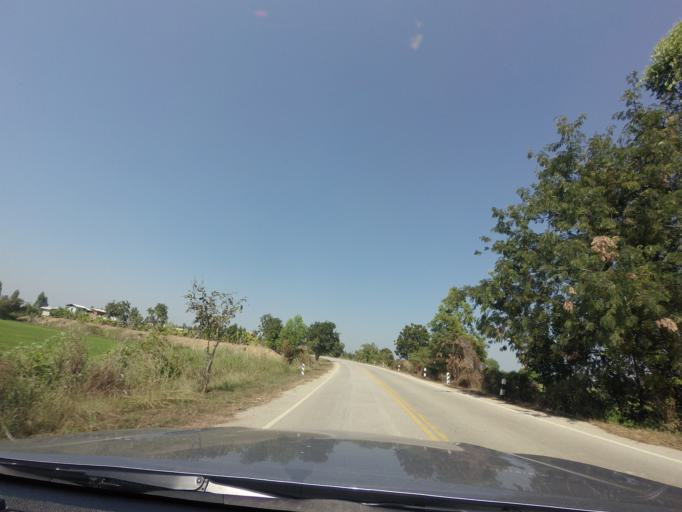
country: TH
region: Sukhothai
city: Sukhothai
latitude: 17.0895
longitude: 99.7904
